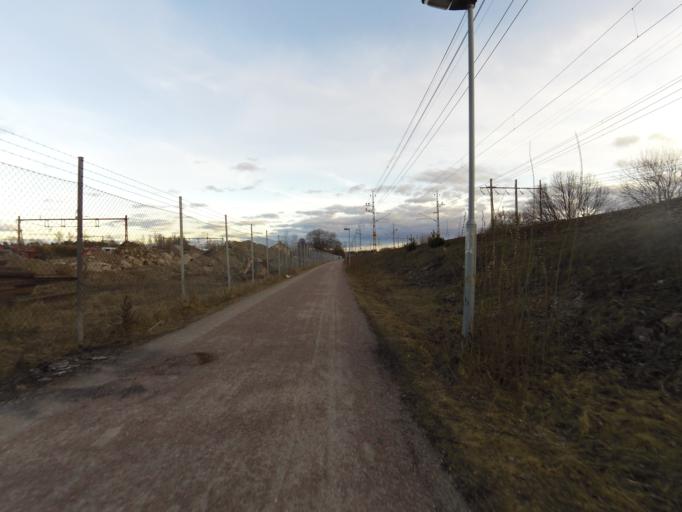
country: SE
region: Gaevleborg
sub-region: Gavle Kommun
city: Gavle
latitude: 60.6646
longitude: 17.1669
